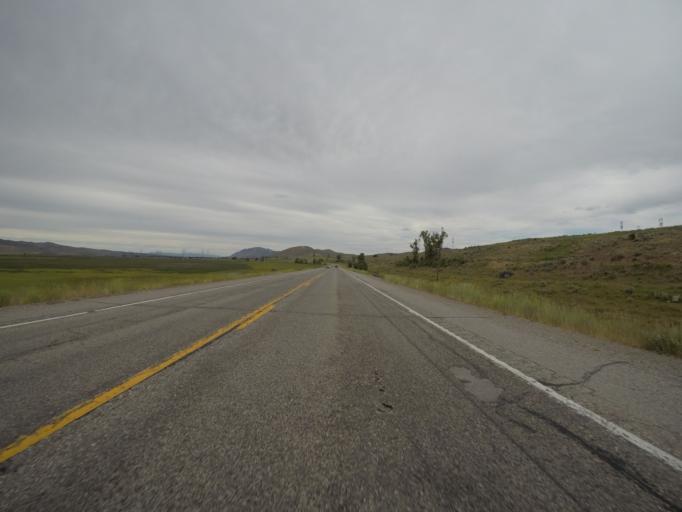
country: US
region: Idaho
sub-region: Bear Lake County
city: Montpelier
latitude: 42.0506
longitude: -110.9313
